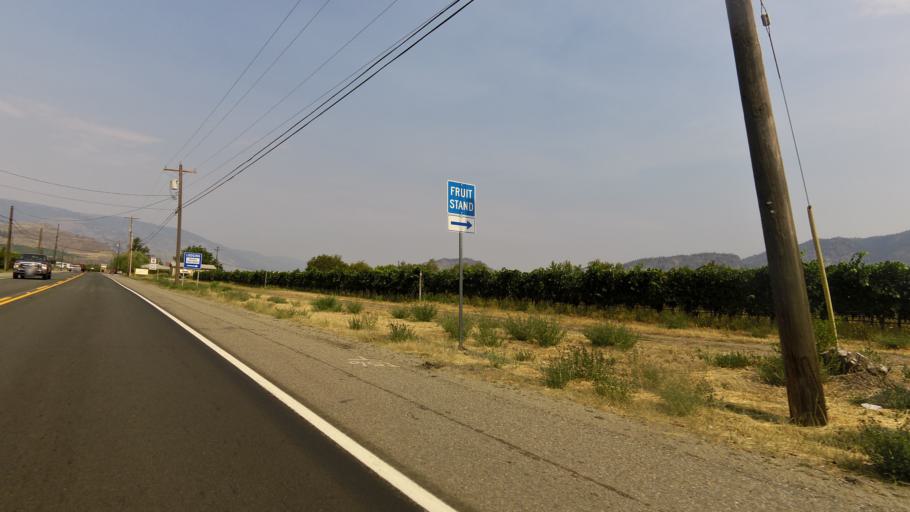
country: CA
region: British Columbia
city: Osoyoos
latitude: 49.0532
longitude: -119.5032
